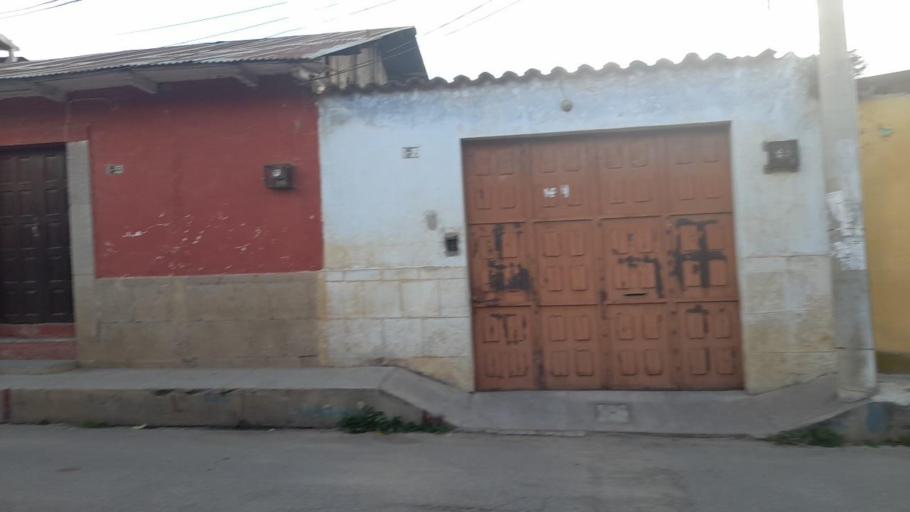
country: GT
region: Quetzaltenango
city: Quetzaltenango
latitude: 14.8300
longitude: -91.5131
